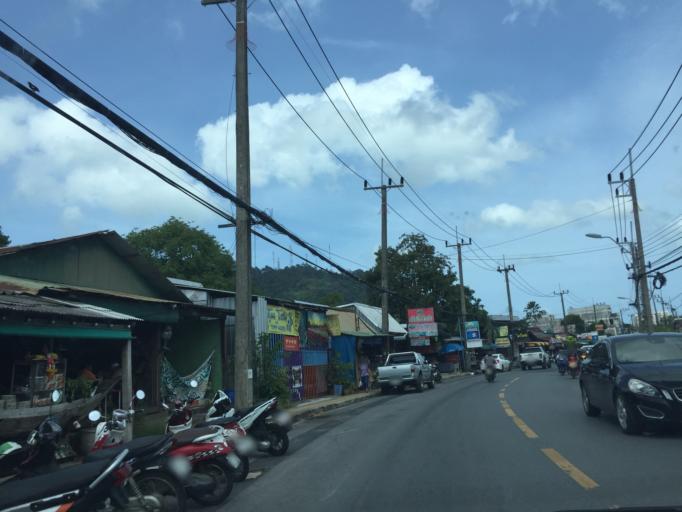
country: TH
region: Phuket
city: Wichit
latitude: 7.9018
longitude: 98.3804
